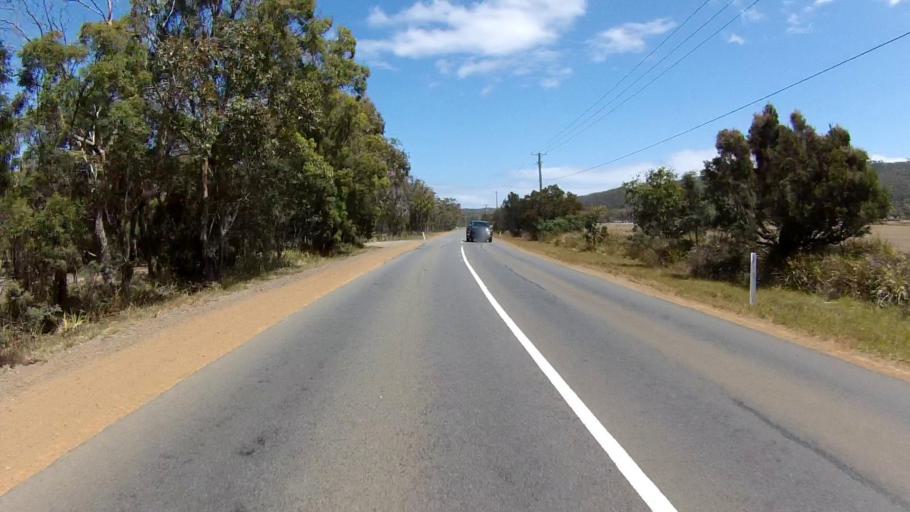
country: AU
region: Tasmania
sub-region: Clarence
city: Sandford
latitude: -42.9413
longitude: 147.4877
